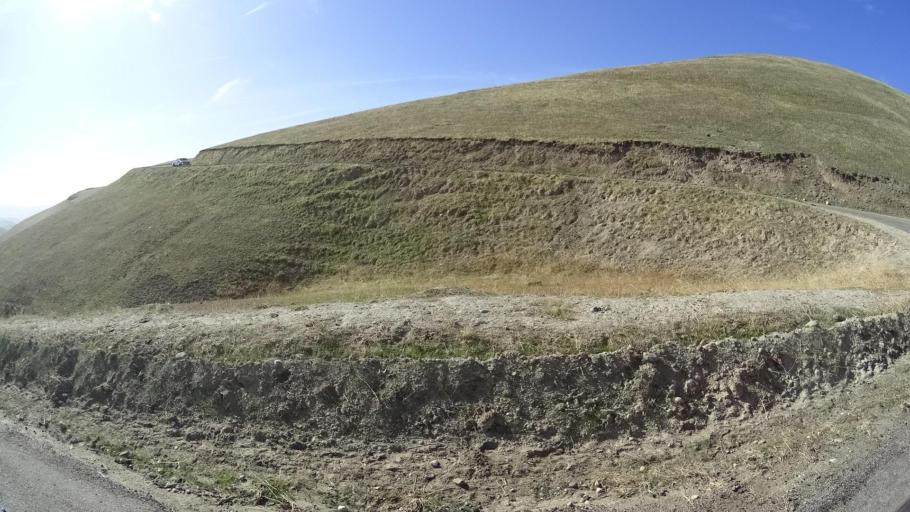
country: US
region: California
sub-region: Kern County
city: Lamont
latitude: 35.4071
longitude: -118.7700
